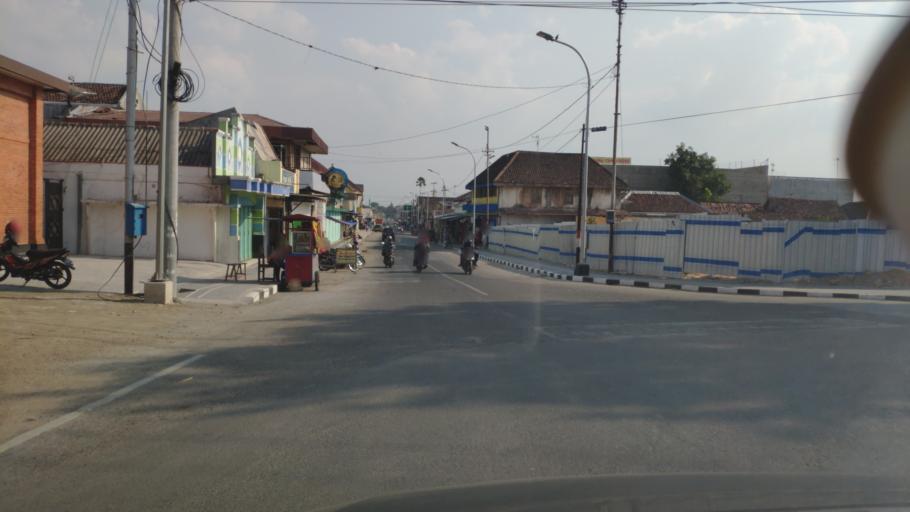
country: ID
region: Central Java
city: Mlangsen
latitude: -6.9706
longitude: 111.4129
